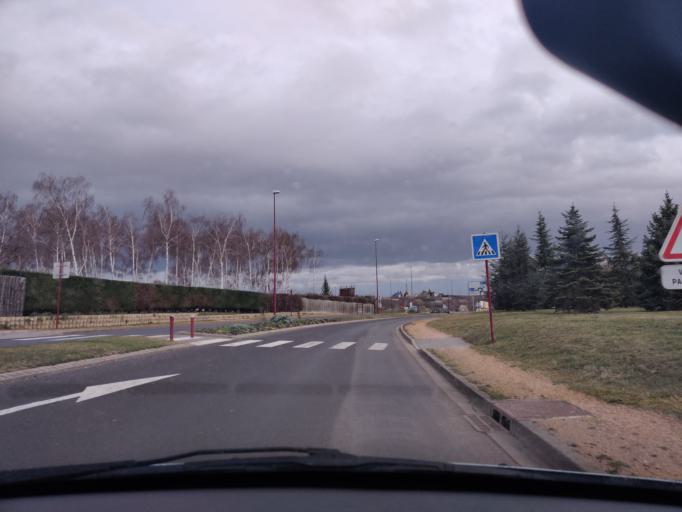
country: FR
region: Auvergne
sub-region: Departement du Puy-de-Dome
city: Chatel-Guyon
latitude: 45.9143
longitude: 3.0780
